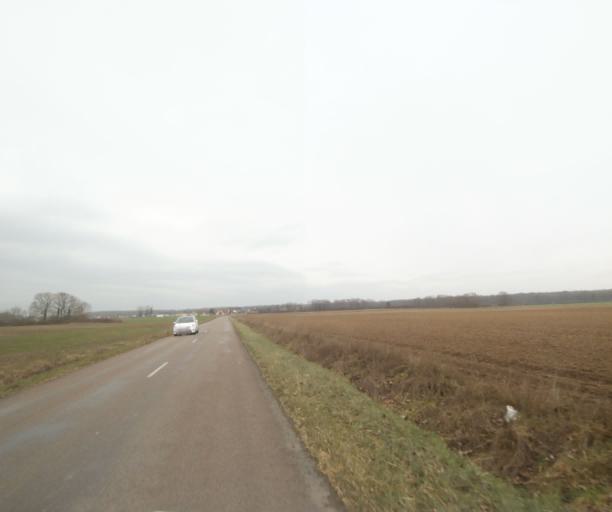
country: FR
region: Champagne-Ardenne
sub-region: Departement de la Haute-Marne
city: Villiers-en-Lieu
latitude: 48.6744
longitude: 4.8894
